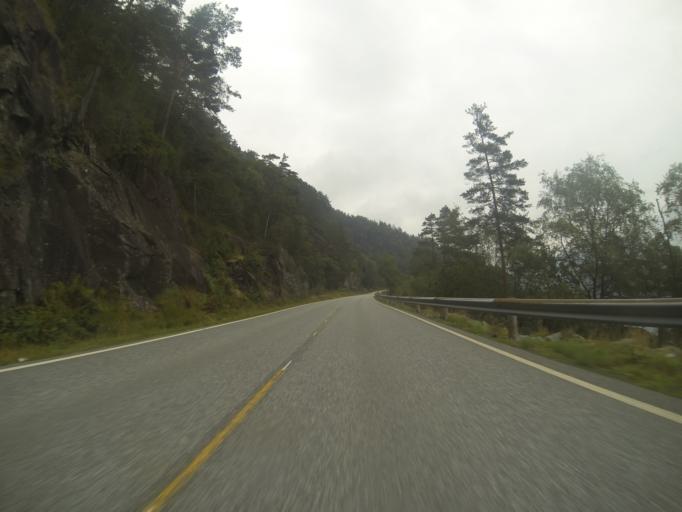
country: NO
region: Rogaland
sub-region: Suldal
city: Sand
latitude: 59.5304
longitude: 6.2493
